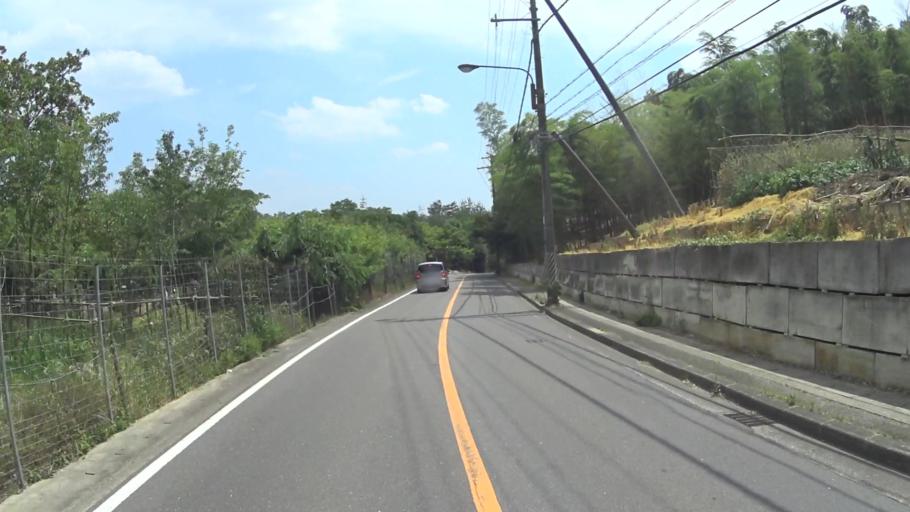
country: JP
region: Kyoto
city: Kyoto
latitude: 35.0291
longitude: 135.6960
